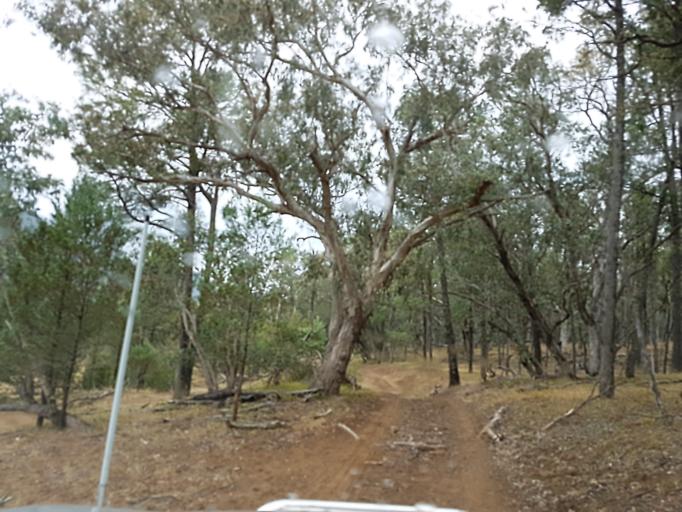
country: AU
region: New South Wales
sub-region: Snowy River
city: Jindabyne
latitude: -36.9496
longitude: 148.3991
